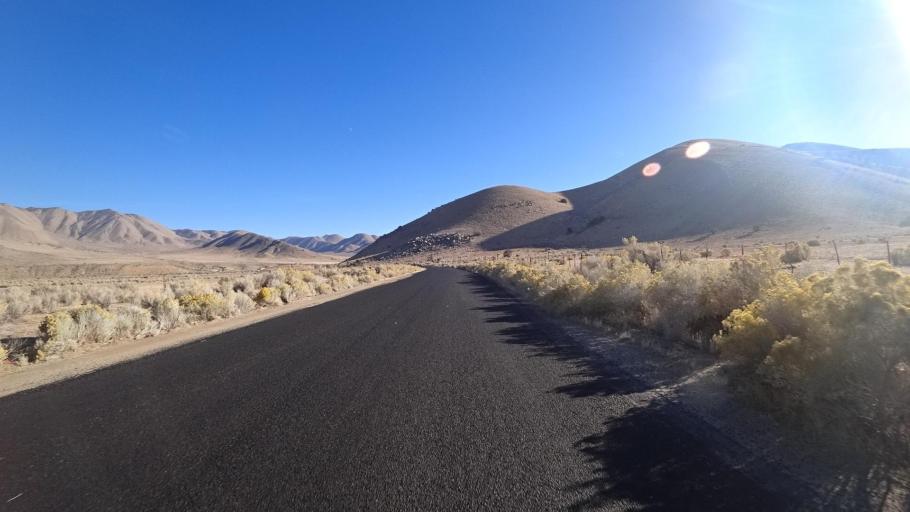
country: US
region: California
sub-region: Kern County
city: Weldon
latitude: 35.6183
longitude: -118.2550
